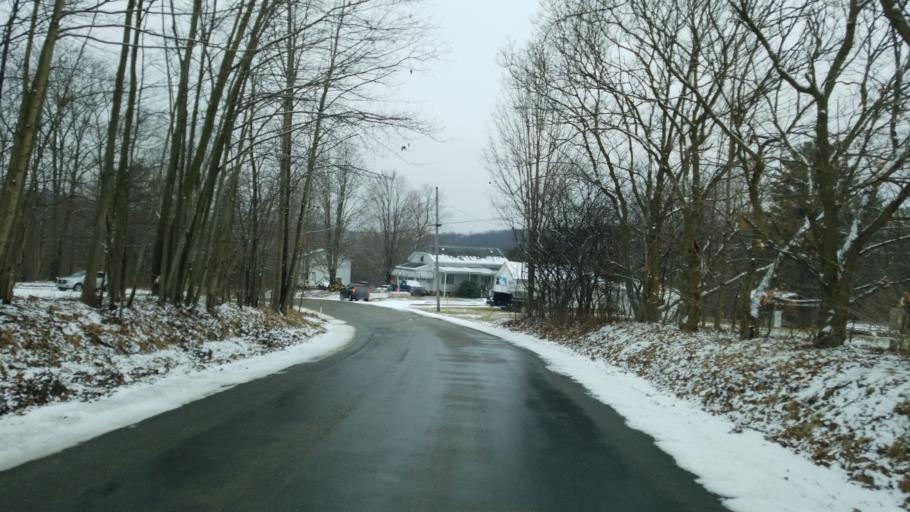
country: US
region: Pennsylvania
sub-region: Jefferson County
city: Reynoldsville
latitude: 41.0883
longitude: -78.8547
